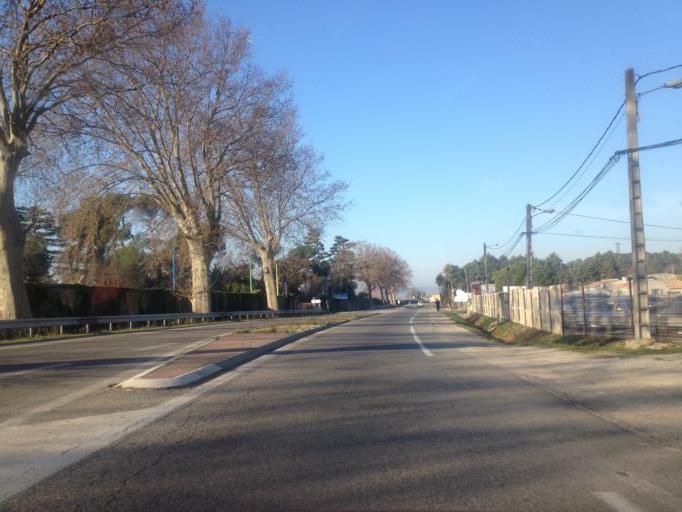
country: FR
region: Provence-Alpes-Cote d'Azur
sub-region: Departement du Vaucluse
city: Piolenc
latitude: 44.1638
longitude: 4.7730
